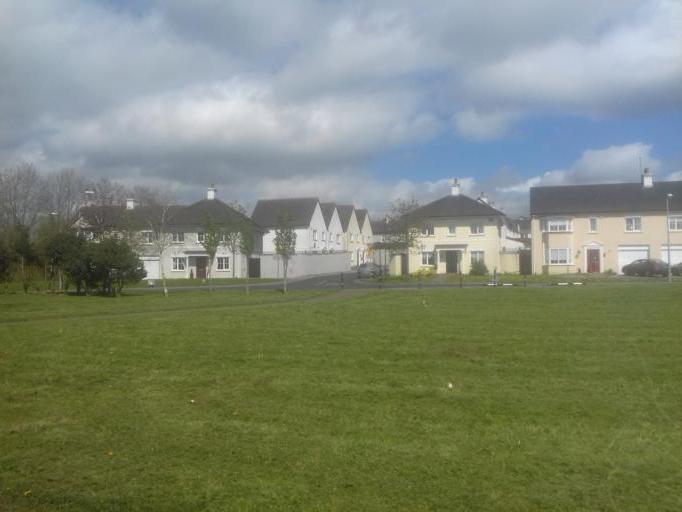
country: IE
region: Leinster
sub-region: Laois
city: Portlaoise
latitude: 53.0435
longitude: -7.2983
